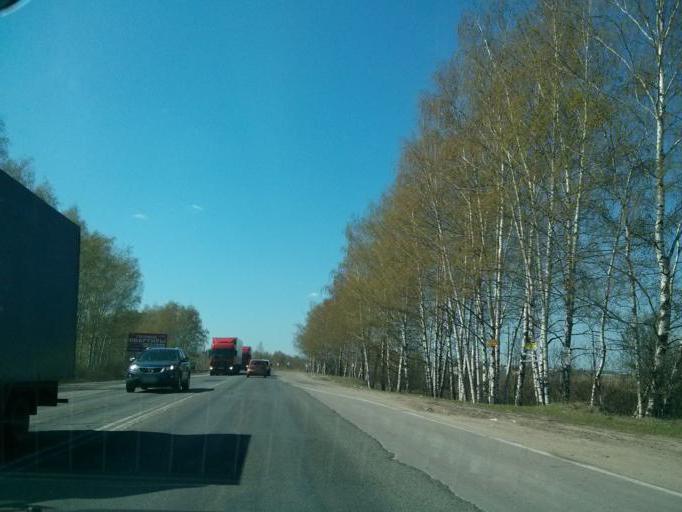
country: RU
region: Nizjnij Novgorod
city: Afonino
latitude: 56.2218
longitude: 44.0602
